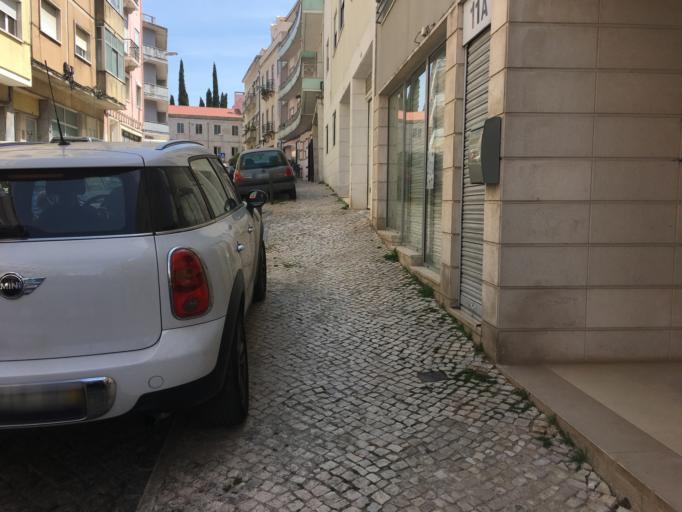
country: PT
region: Lisbon
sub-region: Lisbon
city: Lisbon
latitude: 38.7297
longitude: -9.1632
